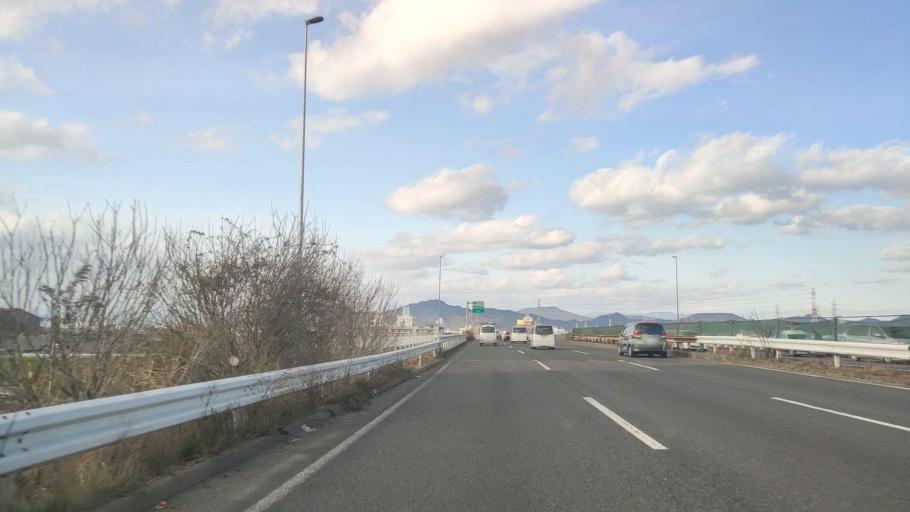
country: JP
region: Gifu
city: Kasamatsucho
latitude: 35.3736
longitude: 136.7839
